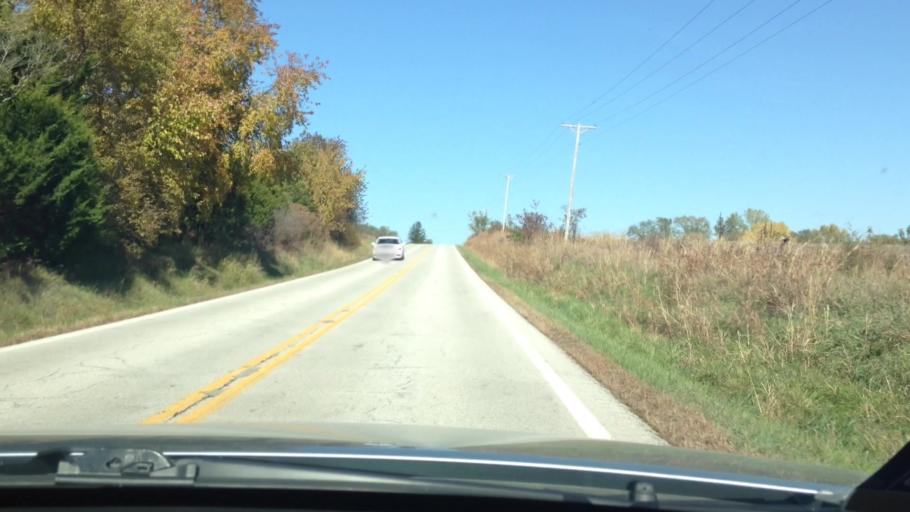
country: US
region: Missouri
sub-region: Clay County
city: Smithville
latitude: 39.3209
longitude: -94.6488
